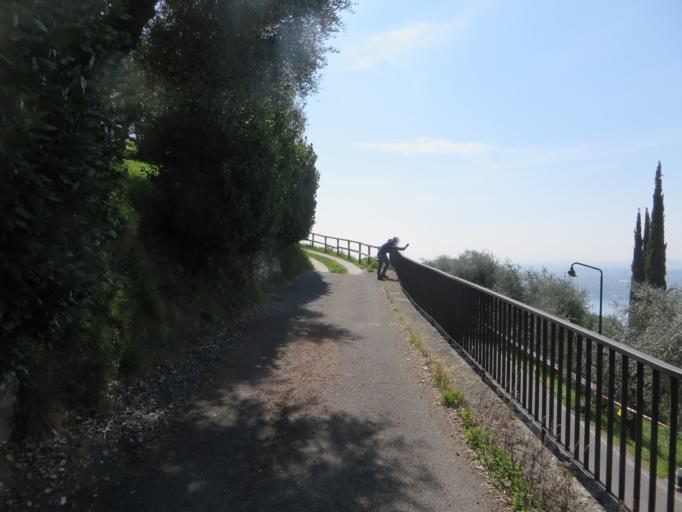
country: IT
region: Lombardy
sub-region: Provincia di Brescia
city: Gardone Riviera
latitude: 45.6303
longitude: 10.5572
